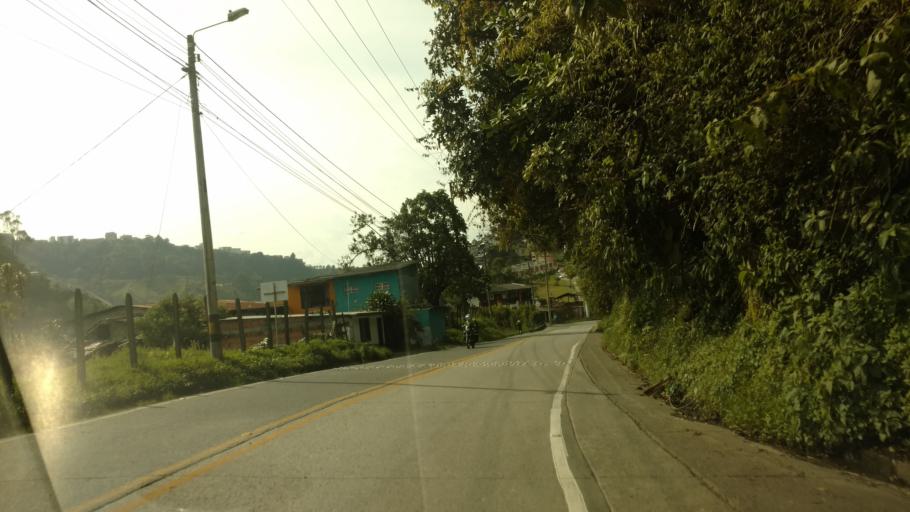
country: CO
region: Caldas
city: Manizales
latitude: 5.0789
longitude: -75.5110
